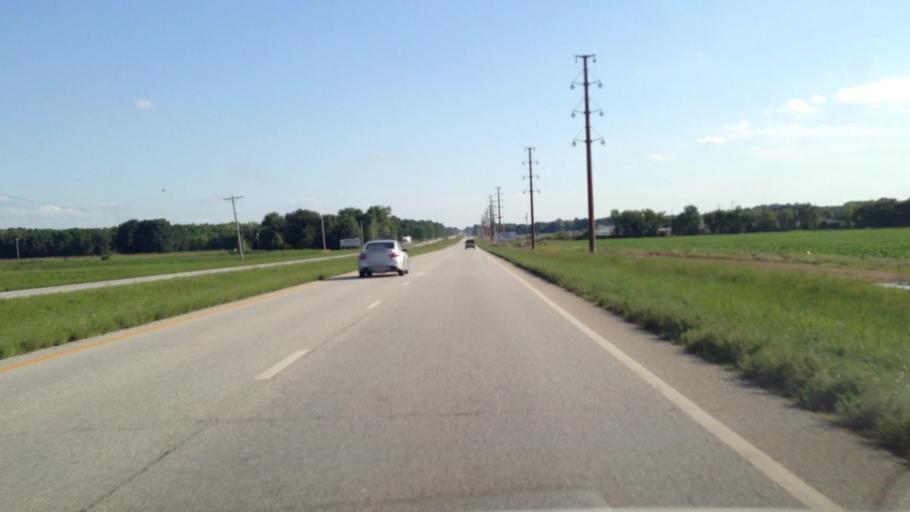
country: US
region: Kansas
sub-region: Crawford County
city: Frontenac
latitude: 37.4876
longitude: -94.7053
